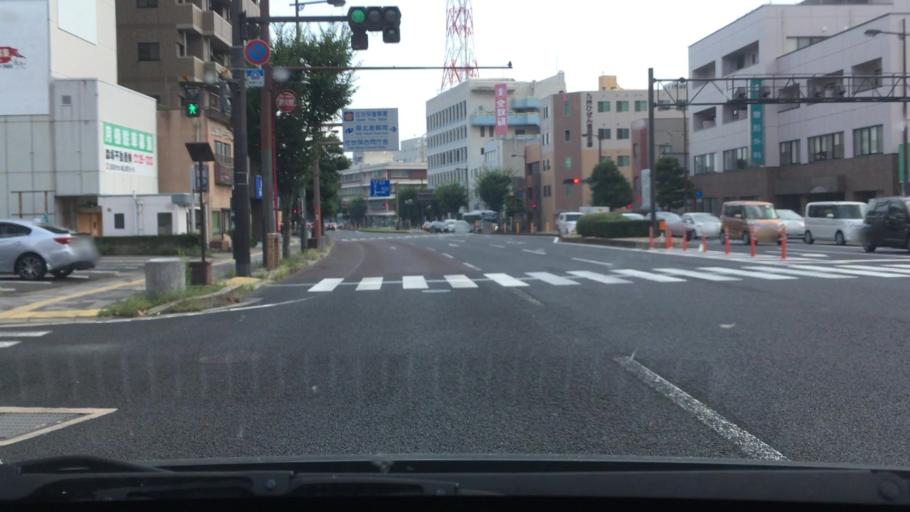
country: JP
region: Nagasaki
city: Sasebo
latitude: 33.1794
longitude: 129.7160
